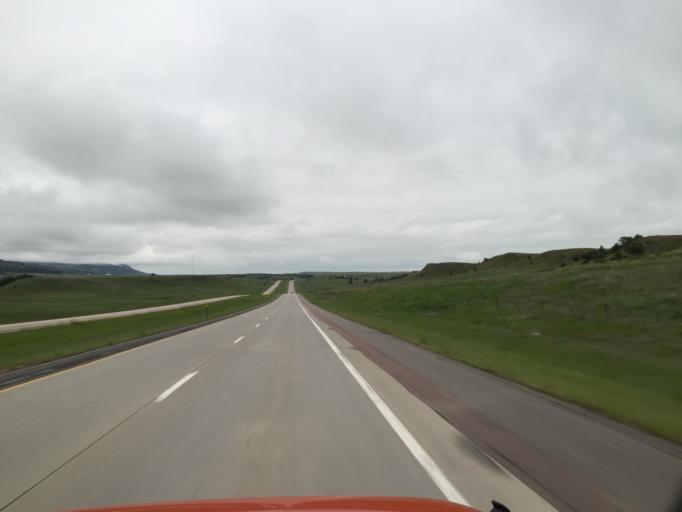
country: US
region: South Dakota
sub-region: Fall River County
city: Hot Springs
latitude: 43.4254
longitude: -103.3817
